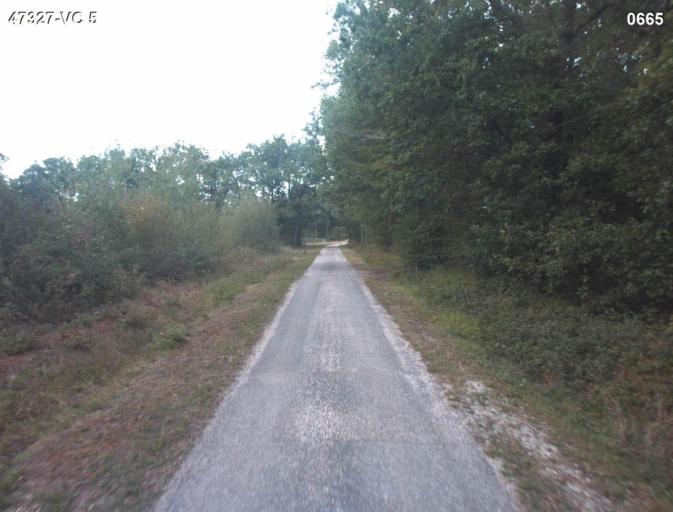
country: FR
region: Aquitaine
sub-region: Departement du Lot-et-Garonne
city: Buzet-sur-Baise
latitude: 44.2224
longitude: 0.2752
